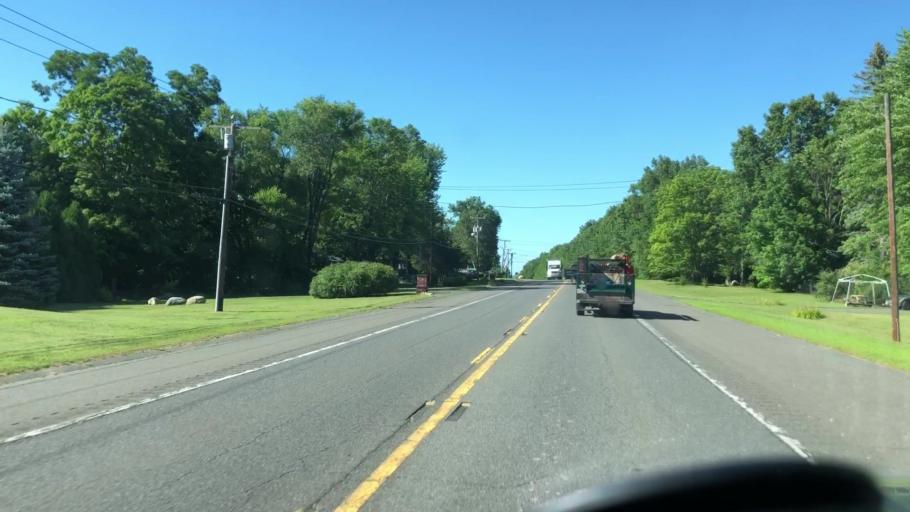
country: US
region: Massachusetts
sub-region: Hampshire County
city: Southampton
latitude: 42.2002
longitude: -72.7265
